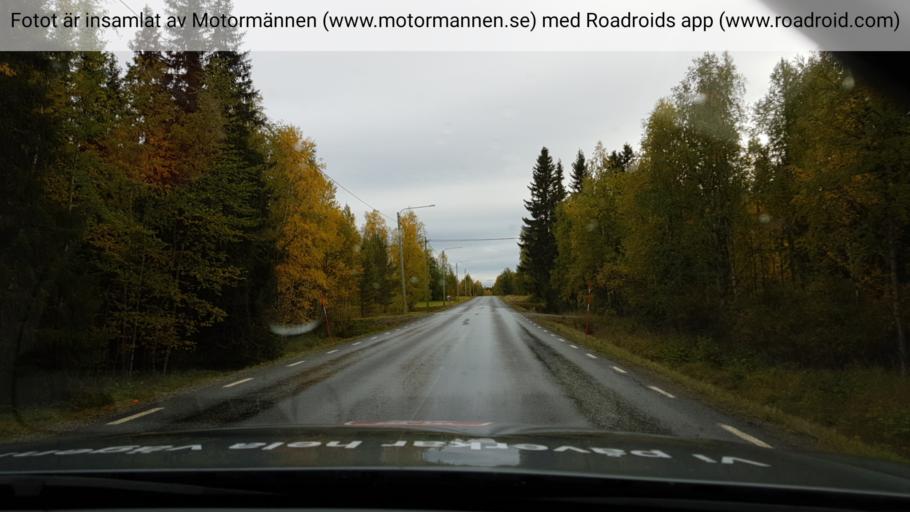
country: SE
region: Vaesterbotten
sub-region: Vilhelmina Kommun
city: Sjoberg
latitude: 64.6826
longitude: 16.2878
